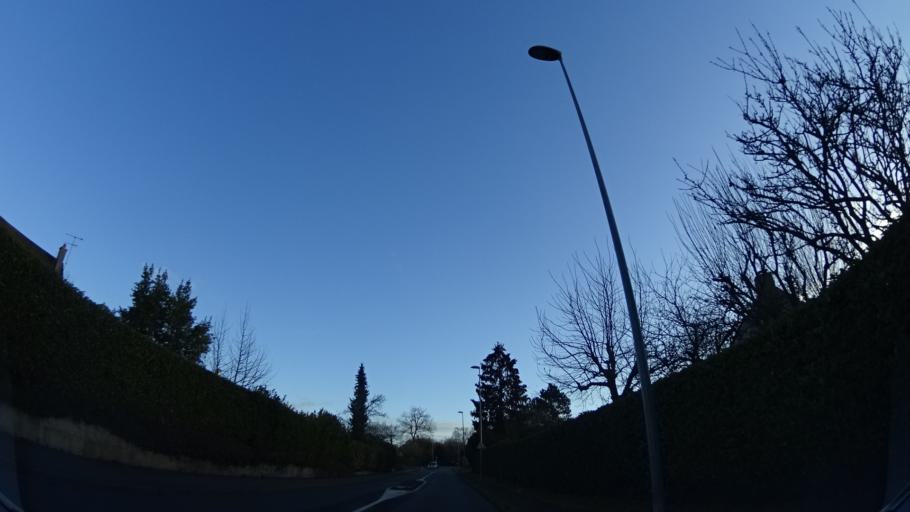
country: FR
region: Brittany
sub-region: Departement d'Ille-et-Vilaine
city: Betton
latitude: 48.1794
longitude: -1.6542
